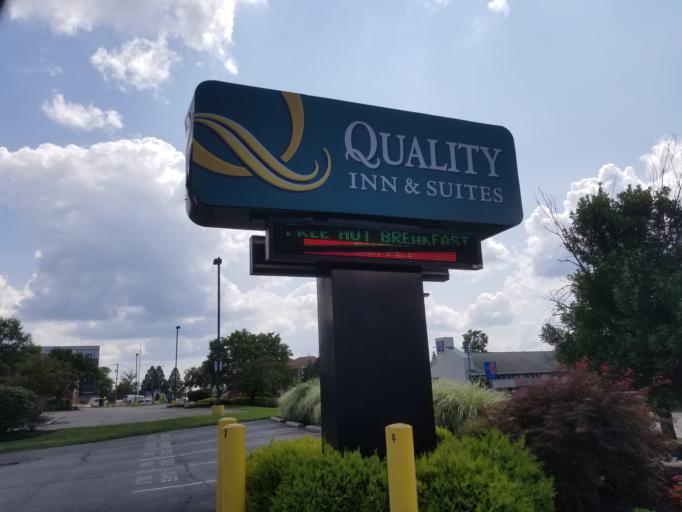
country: US
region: Ohio
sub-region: Franklin County
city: Worthington
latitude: 40.1165
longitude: -83.0143
